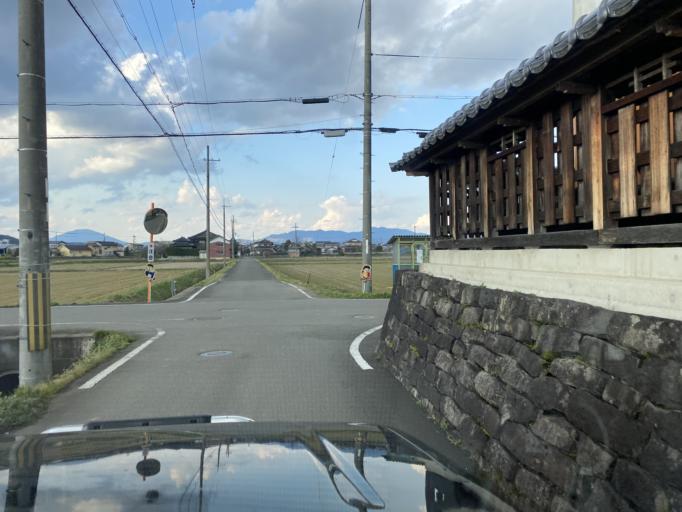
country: JP
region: Hyogo
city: Toyooka
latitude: 35.5062
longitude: 134.8253
